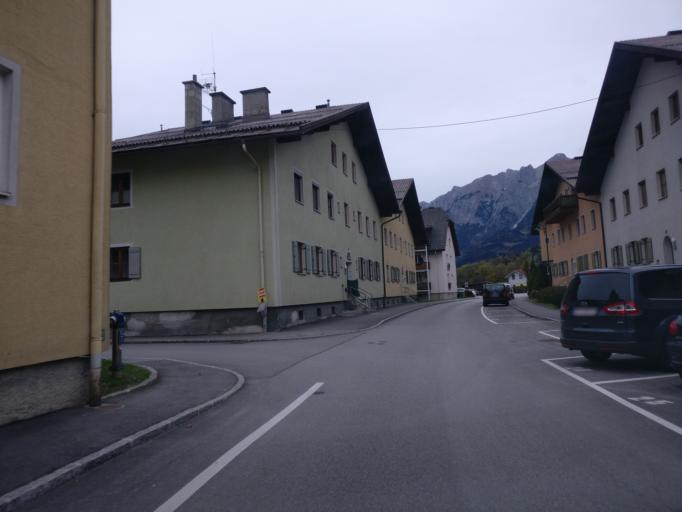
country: AT
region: Salzburg
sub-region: Politischer Bezirk Sankt Johann im Pongau
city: Bischofshofen
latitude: 47.4261
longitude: 13.2171
